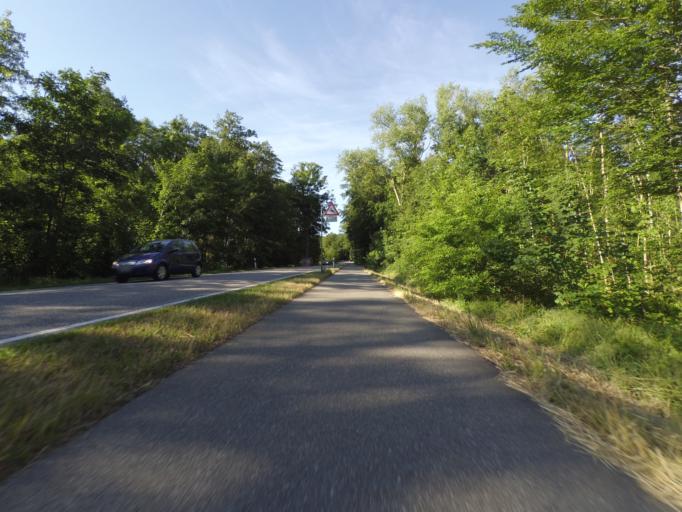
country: DE
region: Mecklenburg-Vorpommern
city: Plau am See
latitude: 53.4429
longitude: 12.2688
